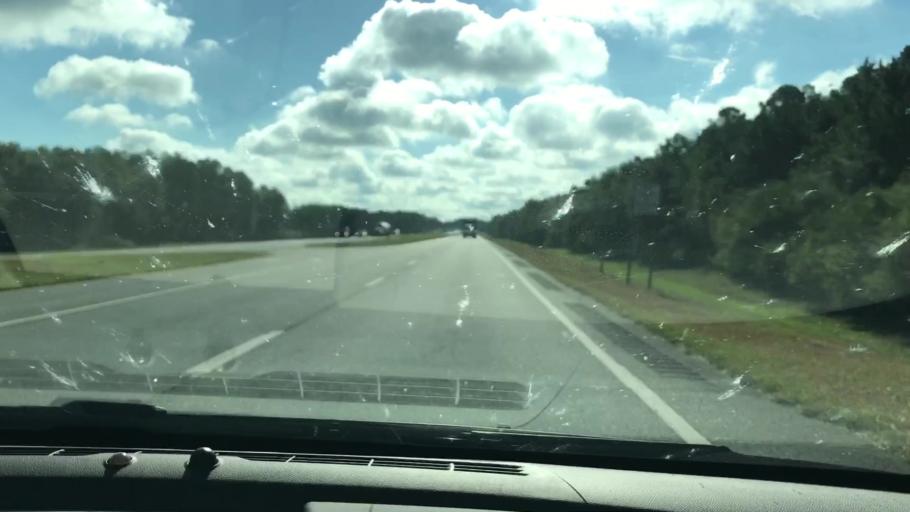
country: US
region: Georgia
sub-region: Worth County
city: Sylvester
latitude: 31.5531
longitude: -83.9819
